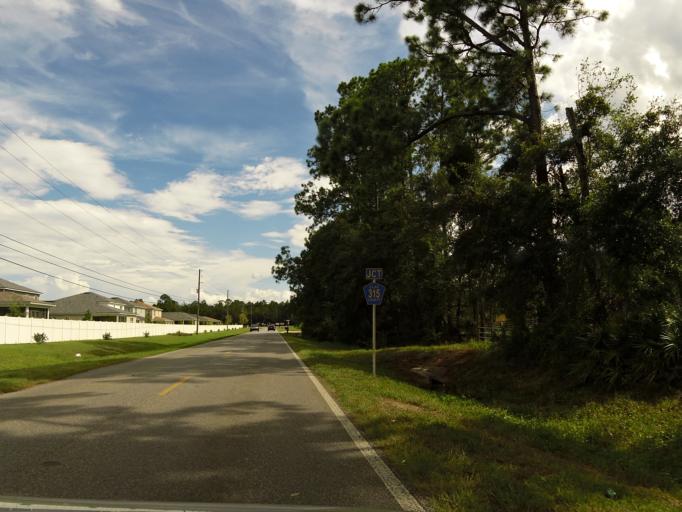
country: US
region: Florida
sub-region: Clay County
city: Green Cove Springs
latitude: 30.0247
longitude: -81.7190
